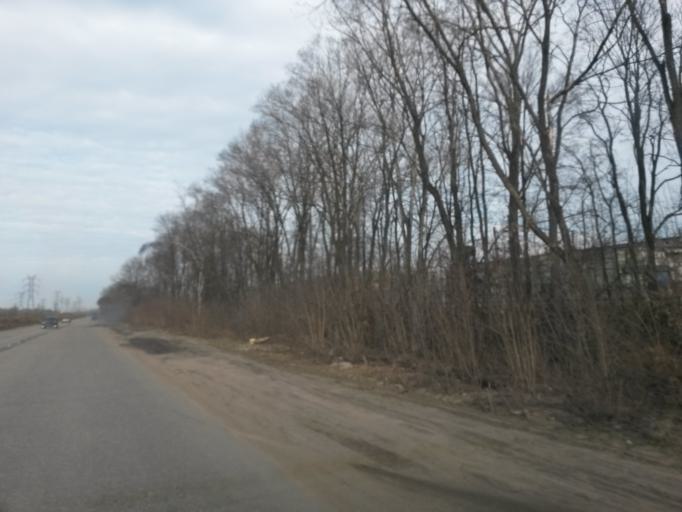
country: RU
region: Jaroslavl
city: Yaroslavl
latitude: 57.6435
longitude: 39.8427
